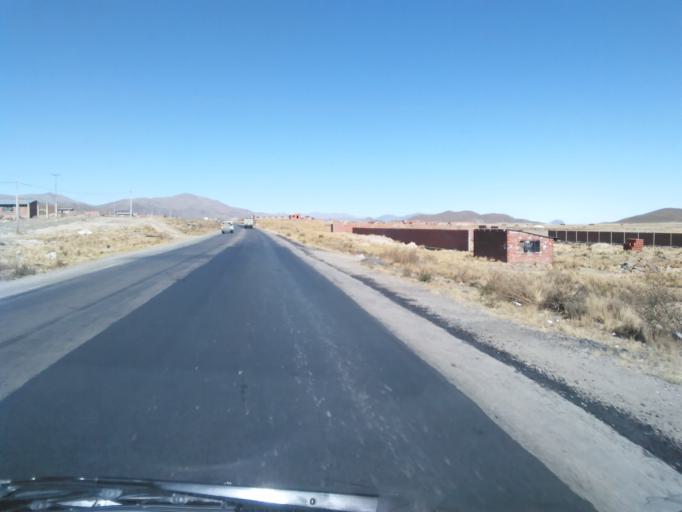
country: BO
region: Oruro
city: Oruro
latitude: -18.0082
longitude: -67.0388
